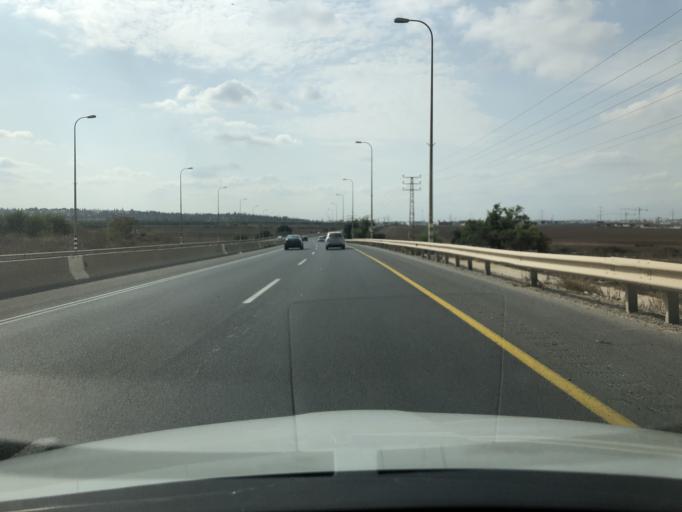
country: IL
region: Central District
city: Et Taiyiba
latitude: 32.2400
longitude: 34.9887
